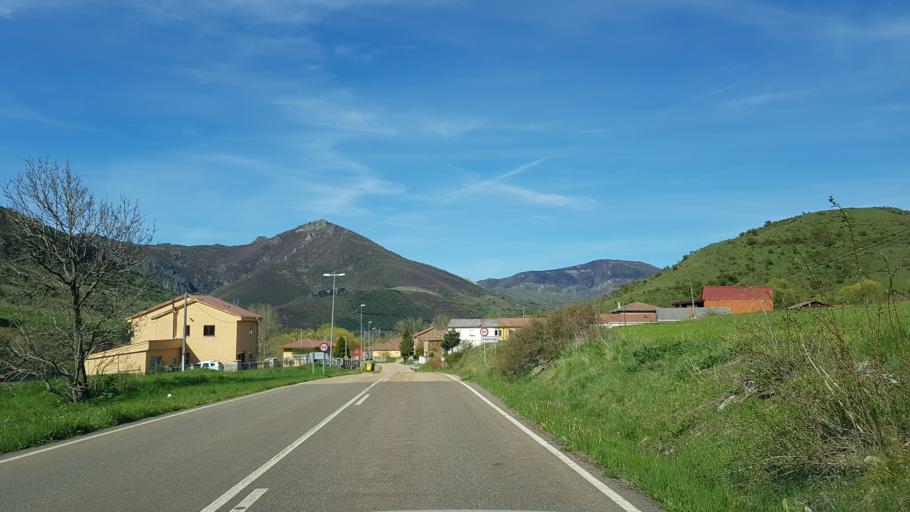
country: ES
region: Castille and Leon
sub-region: Provincia de Leon
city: Villamanin
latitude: 42.9433
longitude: -5.6427
